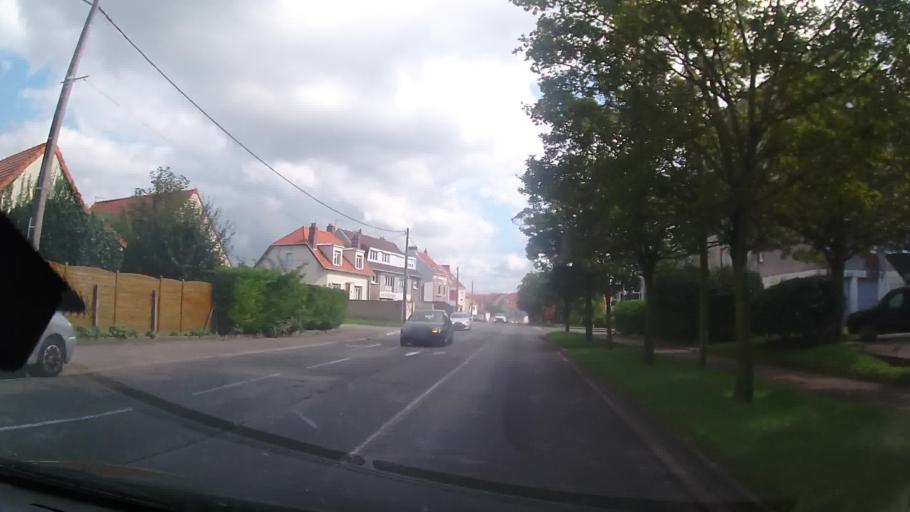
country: FR
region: Nord-Pas-de-Calais
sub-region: Departement du Pas-de-Calais
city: Saint-Martin-Boulogne
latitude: 50.7386
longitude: 1.6186
